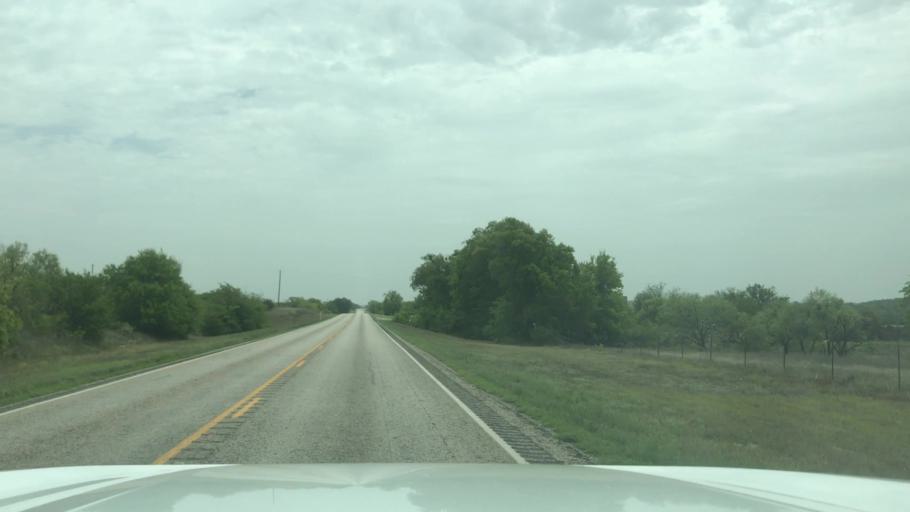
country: US
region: Texas
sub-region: Hamilton County
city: Hico
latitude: 32.0506
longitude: -98.1624
